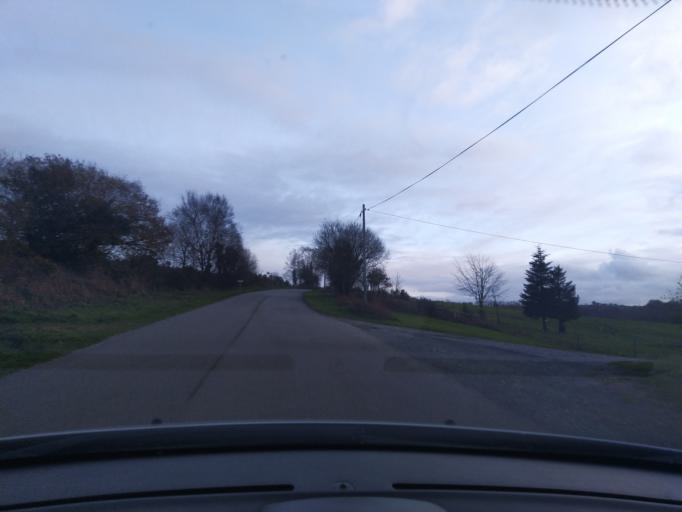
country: FR
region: Brittany
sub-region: Departement du Finistere
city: Guerlesquin
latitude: 48.5270
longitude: -3.6044
